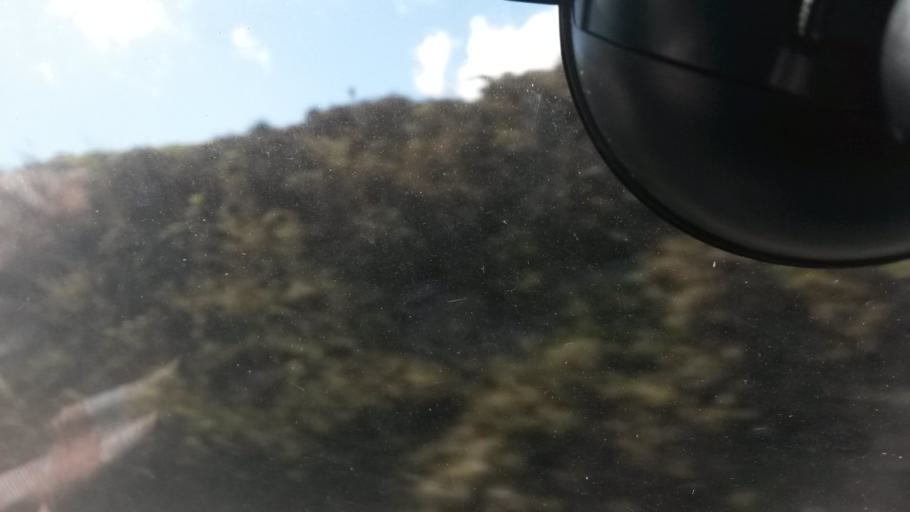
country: IE
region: Munster
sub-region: Ciarrai
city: Dingle
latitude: 52.1603
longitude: -10.2423
